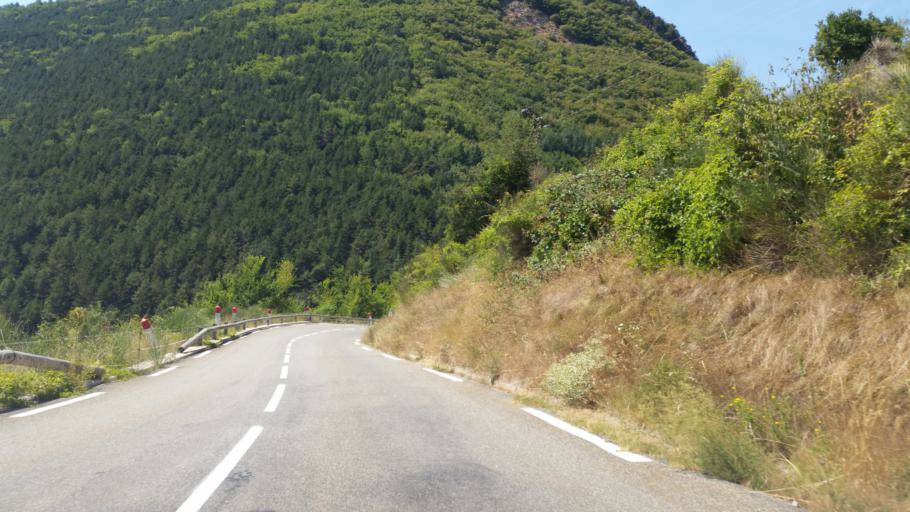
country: FR
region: Provence-Alpes-Cote d'Azur
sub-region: Departement des Alpes-Maritimes
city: Breil-sur-Roya
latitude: 43.9221
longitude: 7.4752
